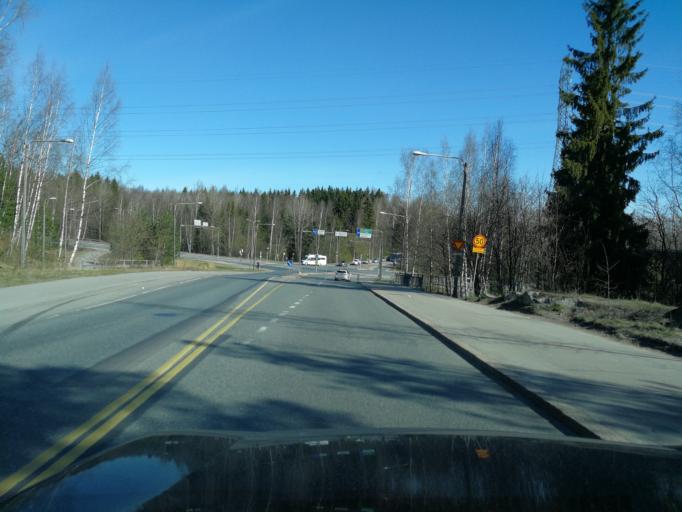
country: FI
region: Uusimaa
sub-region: Helsinki
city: Helsinki
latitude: 60.2196
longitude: 24.9336
